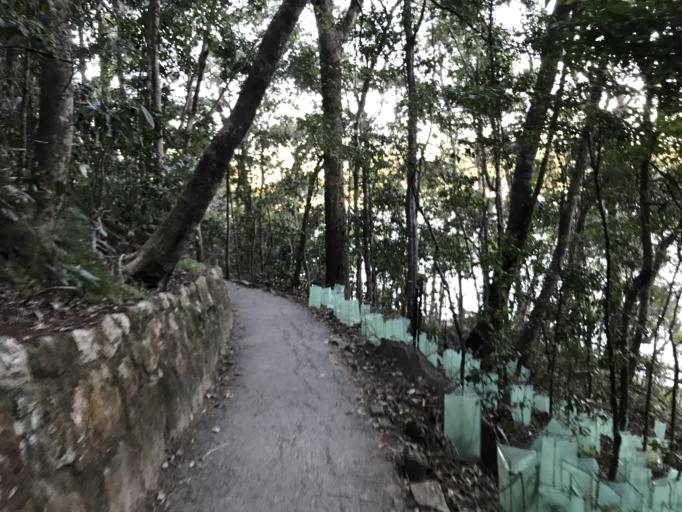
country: AU
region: Queensland
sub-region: Gold Coast
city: Palm Beach
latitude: -28.0964
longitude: 153.4572
